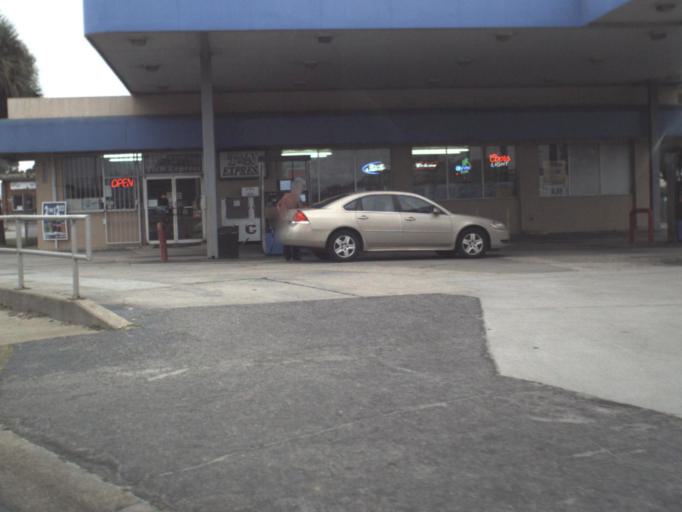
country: US
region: Florida
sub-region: Bay County
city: Pretty Bayou
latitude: 30.1784
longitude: -85.7018
